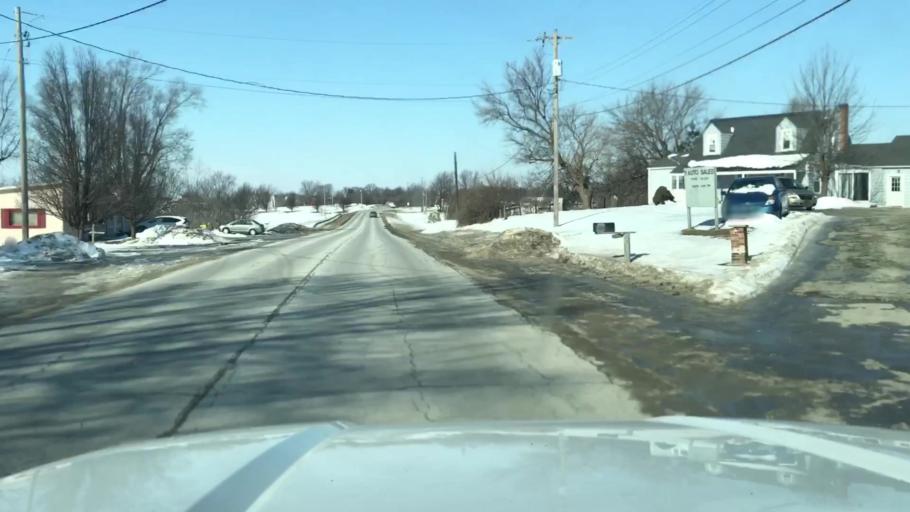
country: US
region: Missouri
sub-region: Andrew County
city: Savannah
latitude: 39.9484
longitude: -94.8415
